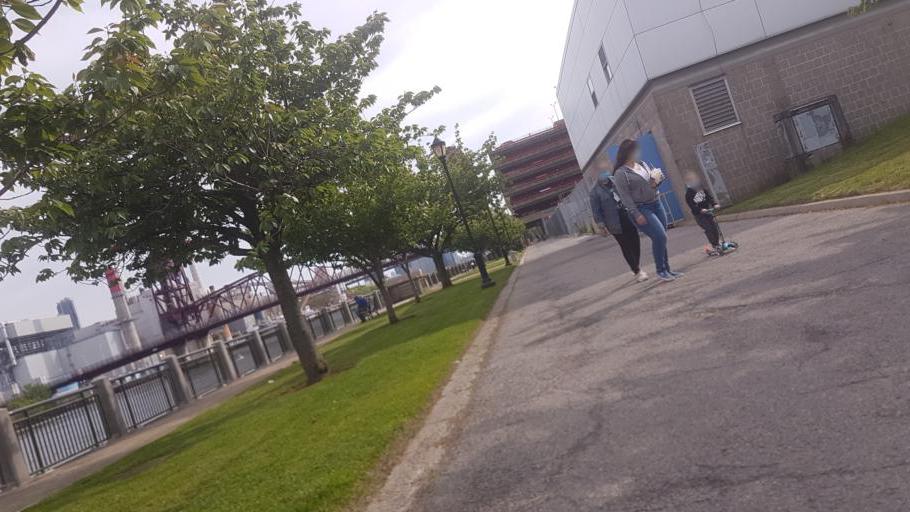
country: US
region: New York
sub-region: Queens County
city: Long Island City
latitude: 40.7662
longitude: -73.9448
